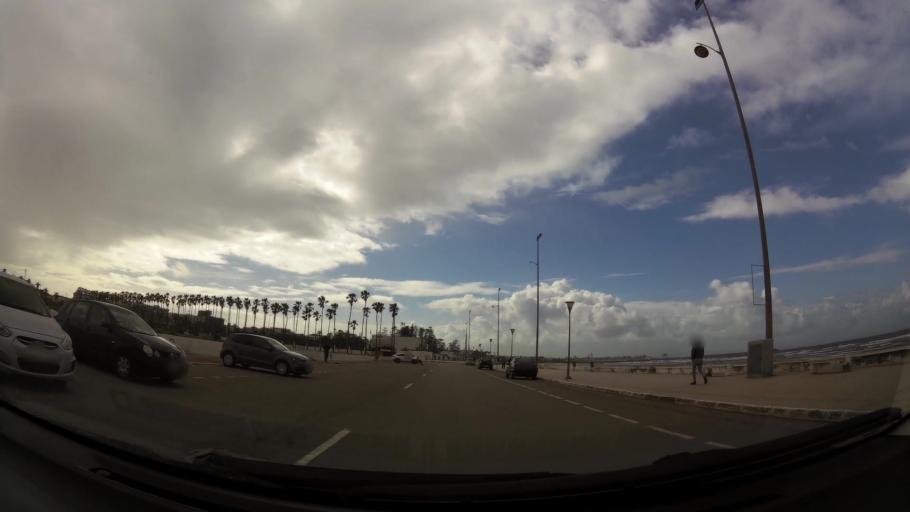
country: MA
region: Doukkala-Abda
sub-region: El-Jadida
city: El Jadida
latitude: 33.2453
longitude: -8.4909
